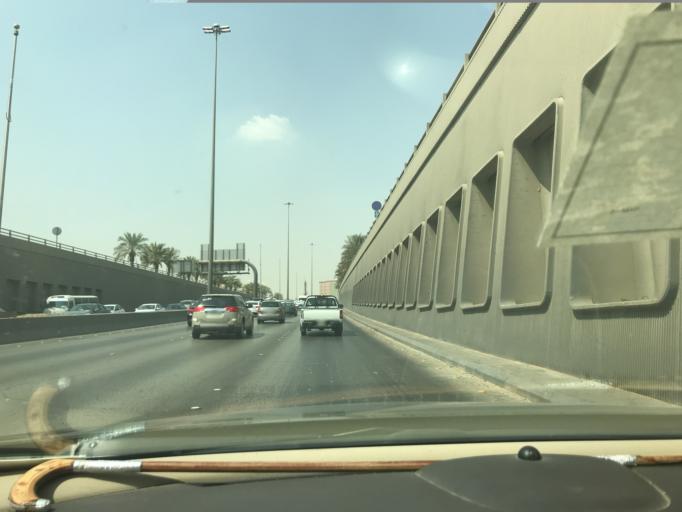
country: SA
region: Ar Riyad
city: Riyadh
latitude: 24.6689
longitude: 46.6952
